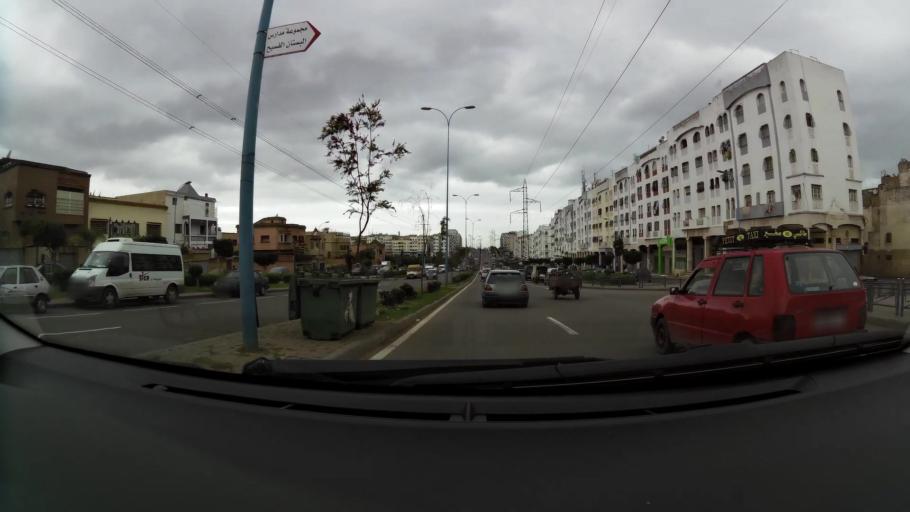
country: MA
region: Grand Casablanca
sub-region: Mediouna
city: Tit Mellil
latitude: 33.5663
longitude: -7.5305
